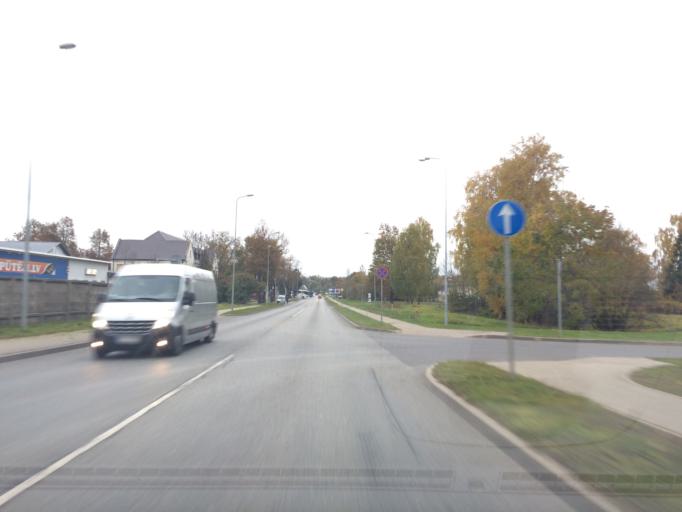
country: LV
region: Jekabpils Rajons
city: Jekabpils
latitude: 56.5182
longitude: 25.8525
